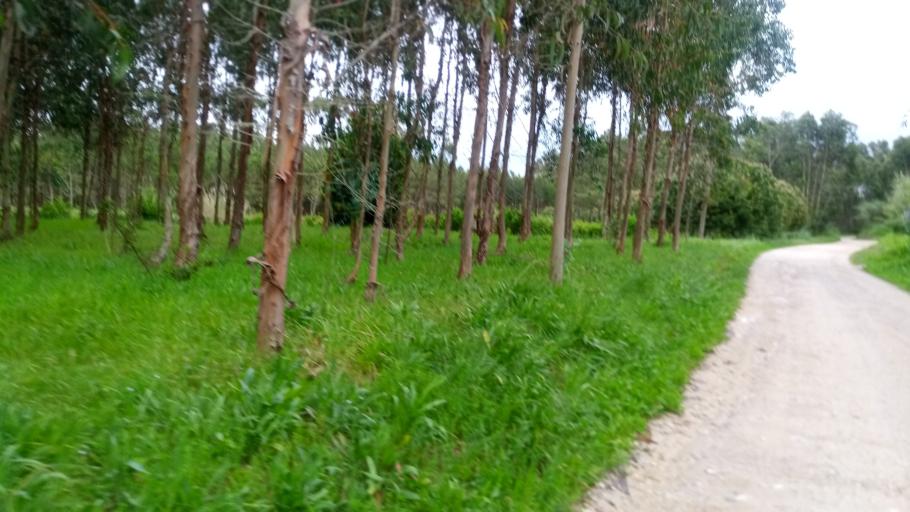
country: PT
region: Leiria
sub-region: Caldas da Rainha
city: Caldas da Rainha
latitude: 39.4504
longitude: -9.1863
